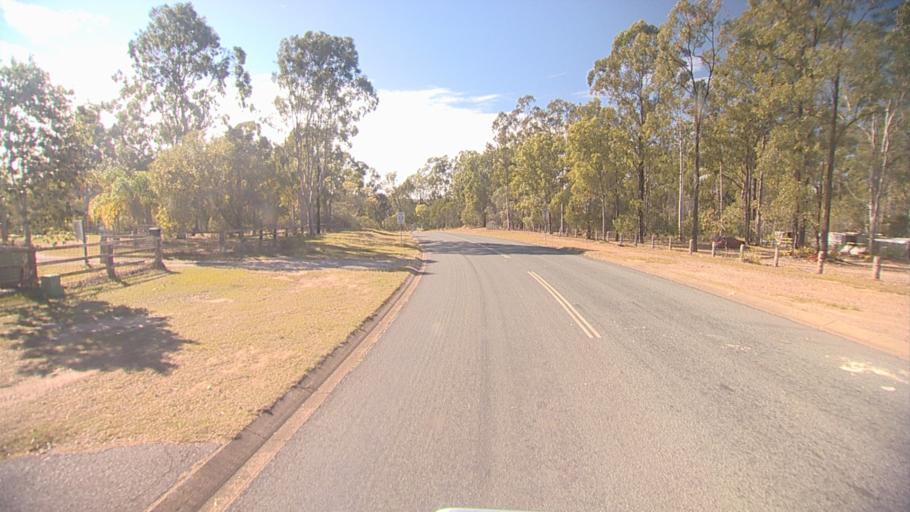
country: AU
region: Queensland
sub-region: Ipswich
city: Springfield Lakes
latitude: -27.7110
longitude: 152.9330
